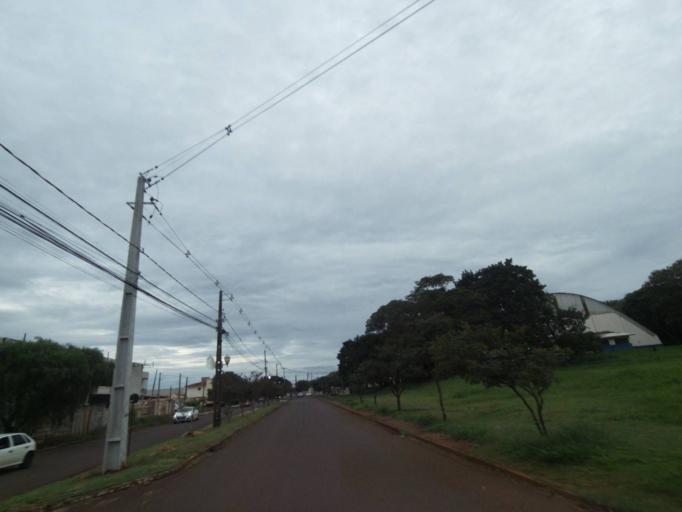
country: BR
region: Parana
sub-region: Campo Mourao
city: Campo Mourao
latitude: -24.0384
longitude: -52.3638
